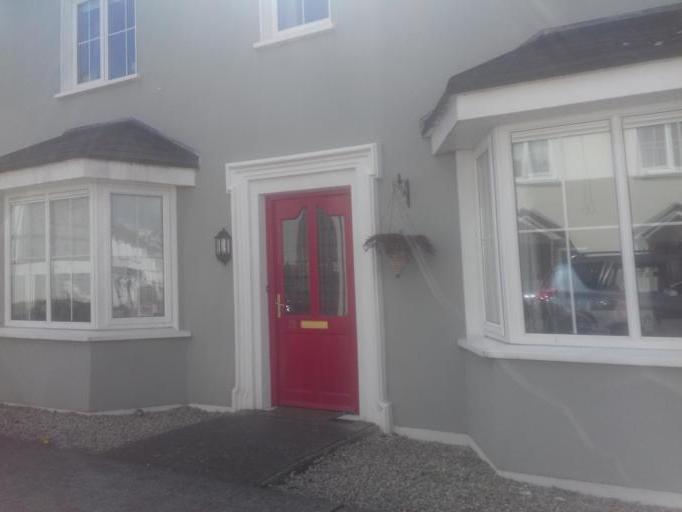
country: IE
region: Leinster
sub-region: Laois
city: Portlaoise
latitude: 53.0411
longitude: -7.2993
